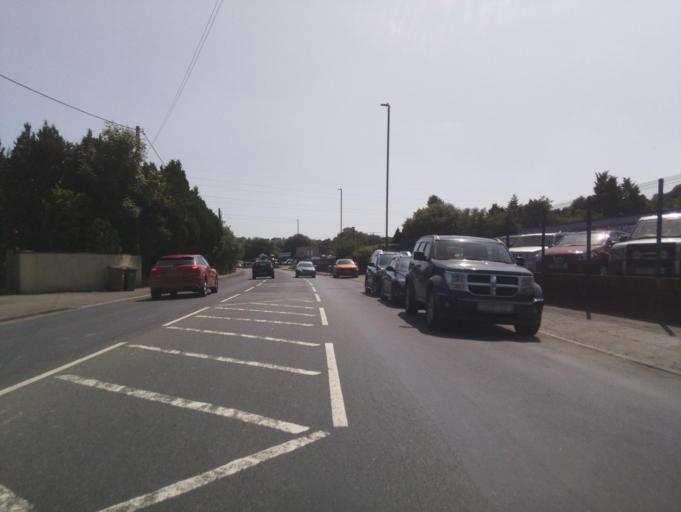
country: GB
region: Wales
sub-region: Caerphilly County Borough
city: Pengam
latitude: 51.6665
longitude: -3.2298
